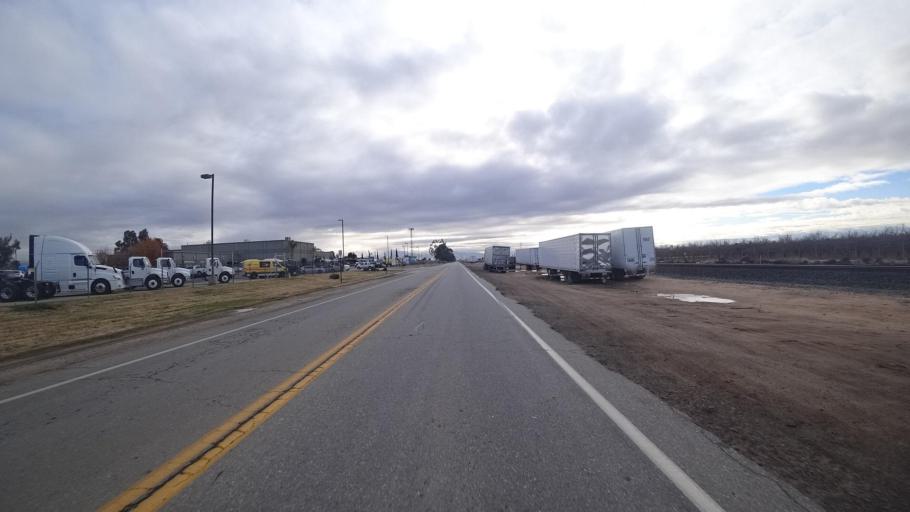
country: US
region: California
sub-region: Kern County
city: Greenacres
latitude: 35.4357
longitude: -119.0798
